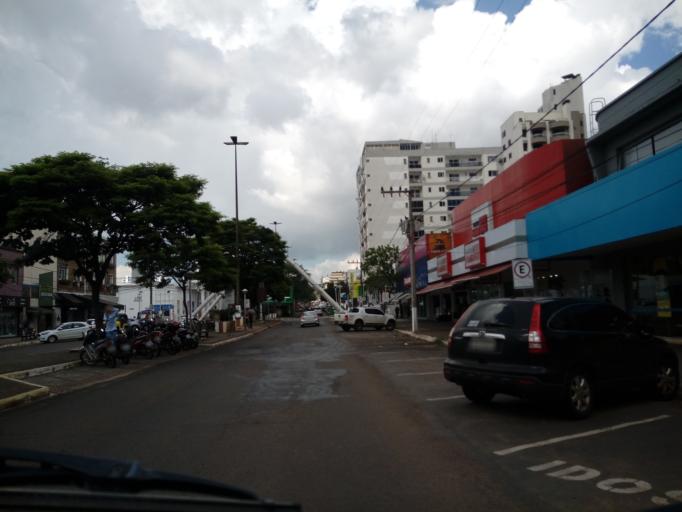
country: BR
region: Santa Catarina
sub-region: Chapeco
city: Chapeco
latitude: -27.0984
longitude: -52.6161
